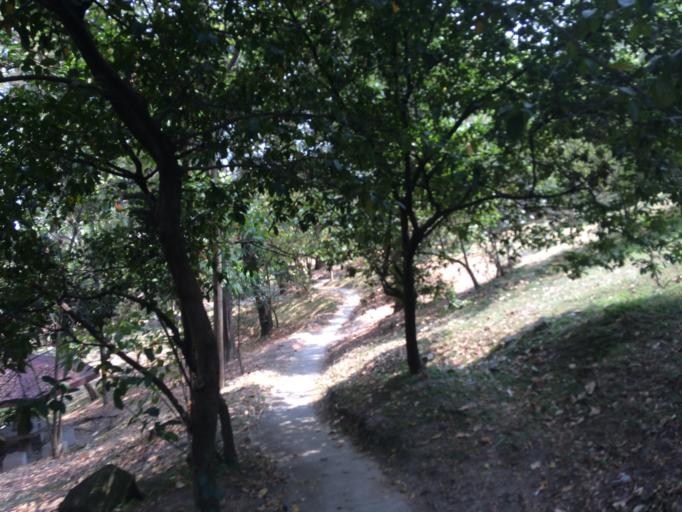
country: CO
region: Antioquia
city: Medellin
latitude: 6.2363
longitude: -75.5790
